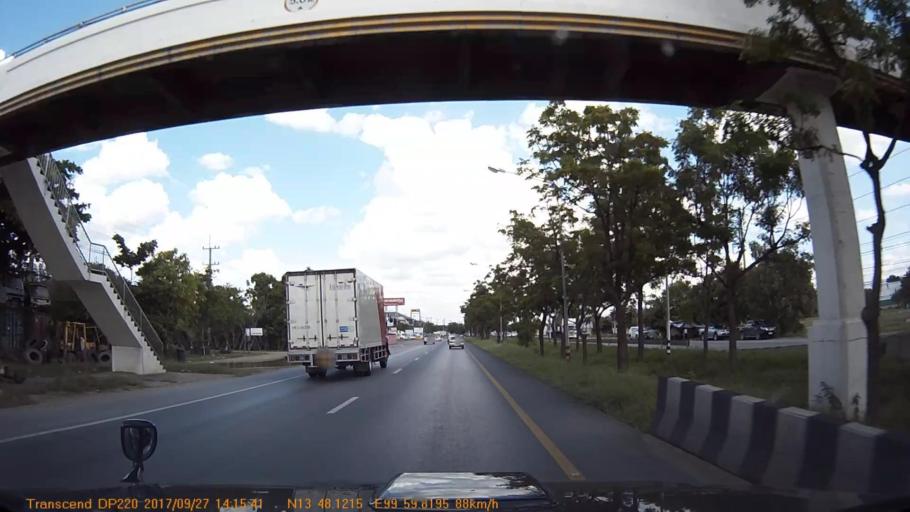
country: TH
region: Nakhon Pathom
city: Nakhon Pathom
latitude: 13.8020
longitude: 99.9969
